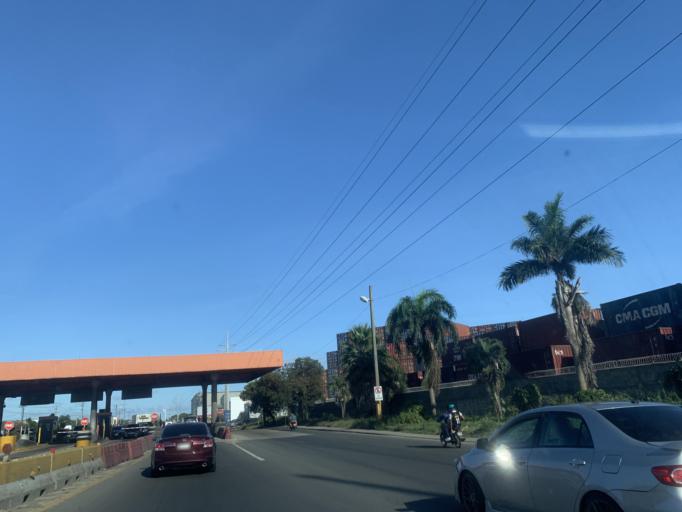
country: DO
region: San Cristobal
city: El Carril
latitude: 18.4292
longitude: -70.0015
